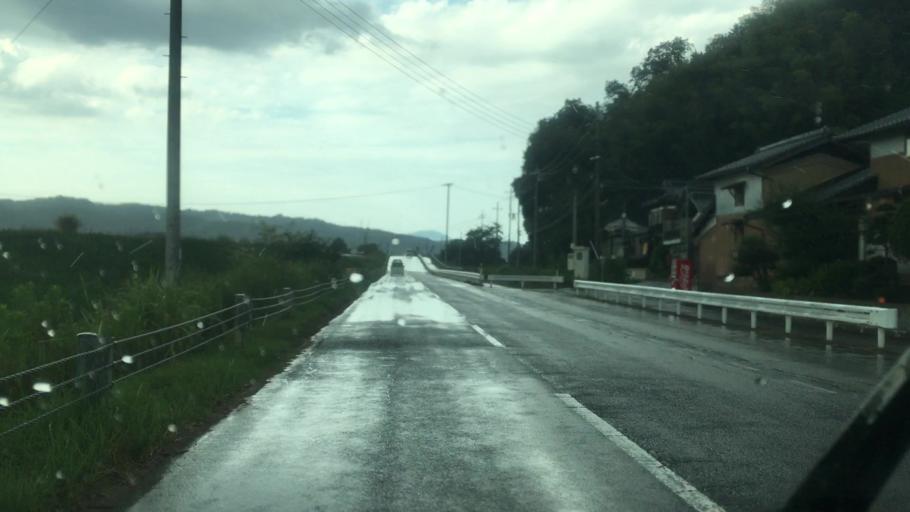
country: JP
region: Hyogo
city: Toyooka
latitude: 35.4866
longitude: 134.8170
